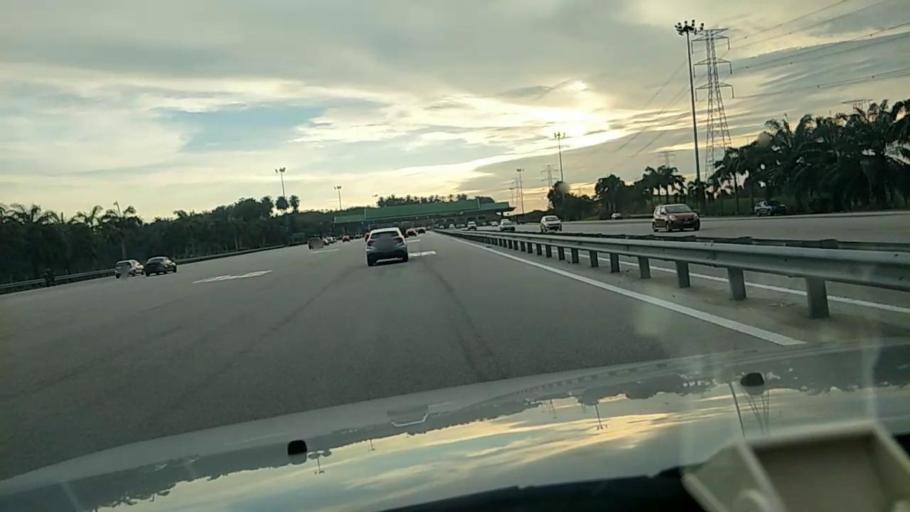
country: MY
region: Selangor
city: Shah Alam
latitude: 3.0918
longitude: 101.4896
